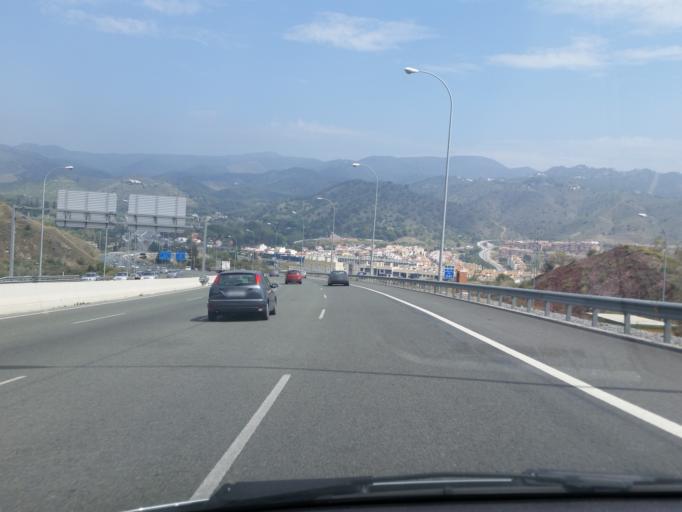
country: ES
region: Andalusia
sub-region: Provincia de Malaga
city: Malaga
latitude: 36.7486
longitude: -4.4334
